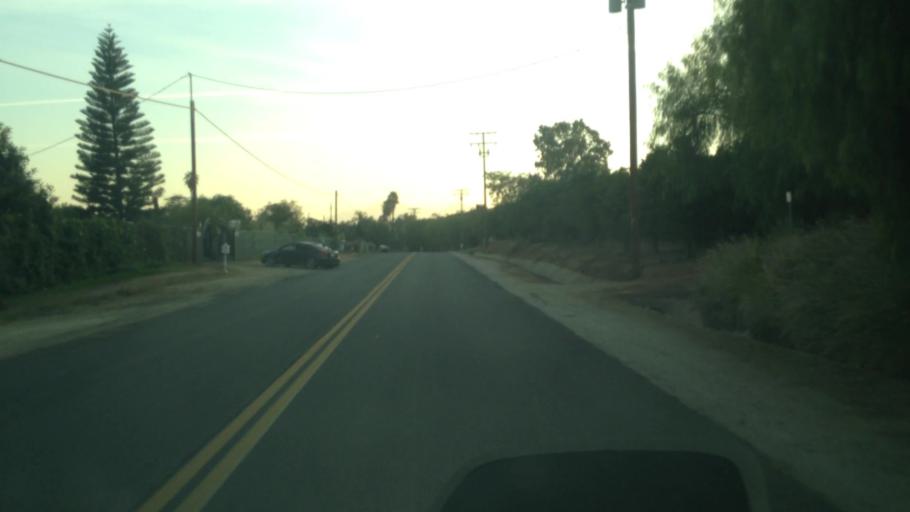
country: US
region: California
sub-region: Riverside County
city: Woodcrest
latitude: 33.8692
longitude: -117.4378
